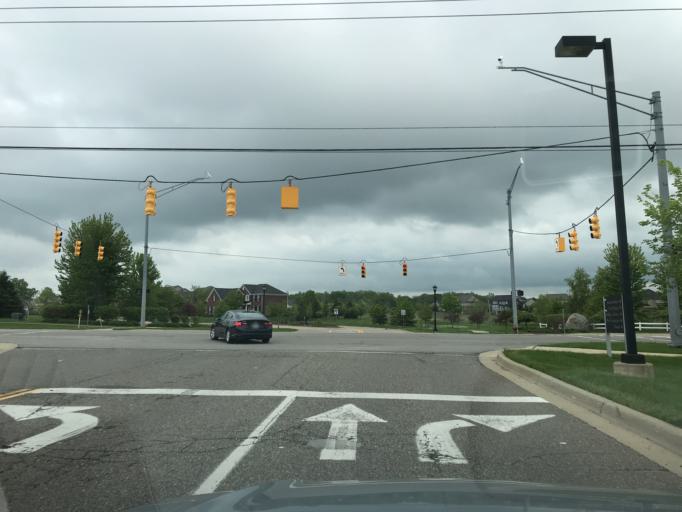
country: US
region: Michigan
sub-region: Oakland County
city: Wixom
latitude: 42.4640
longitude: -83.5685
